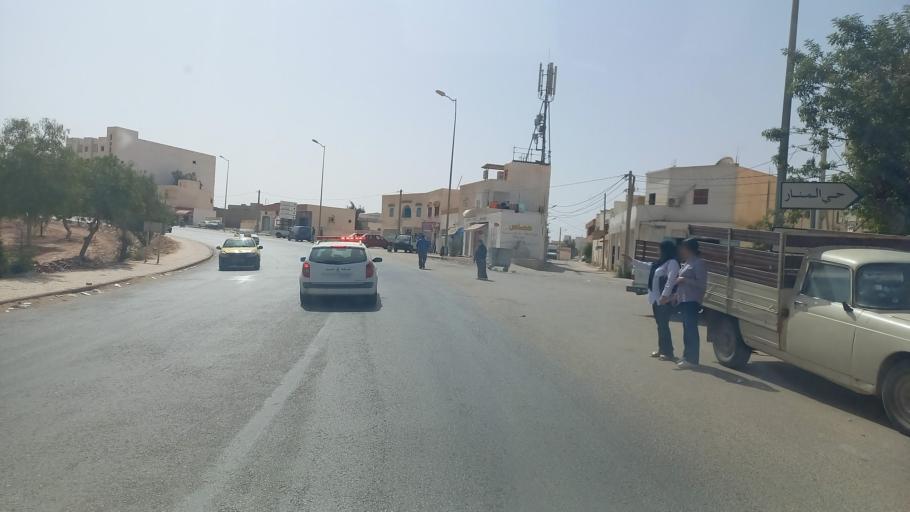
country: TN
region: Madanin
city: Medenine
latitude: 33.3424
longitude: 10.5038
